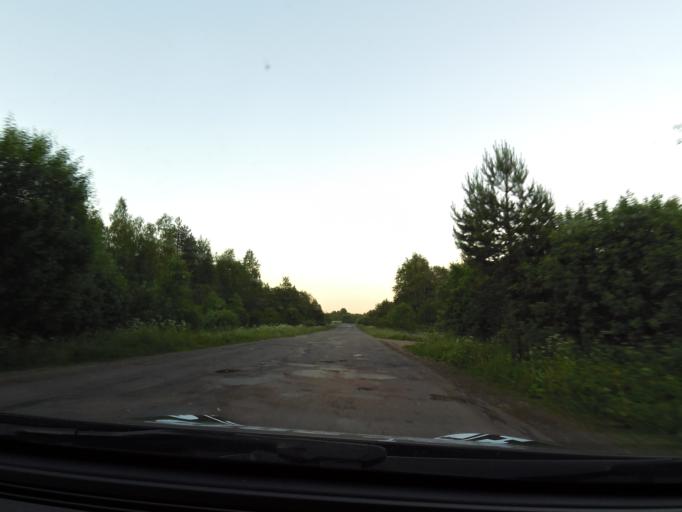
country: RU
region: Leningrad
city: Voznesen'ye
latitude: 60.8486
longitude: 35.5896
